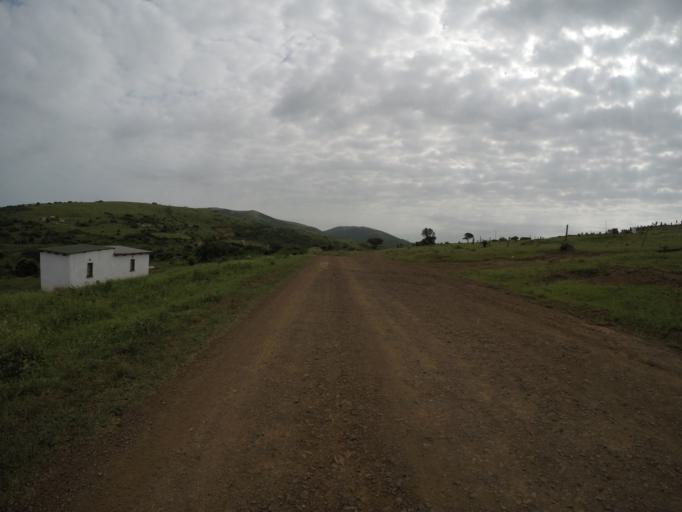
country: ZA
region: KwaZulu-Natal
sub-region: uThungulu District Municipality
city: Empangeni
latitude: -28.6312
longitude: 31.9053
